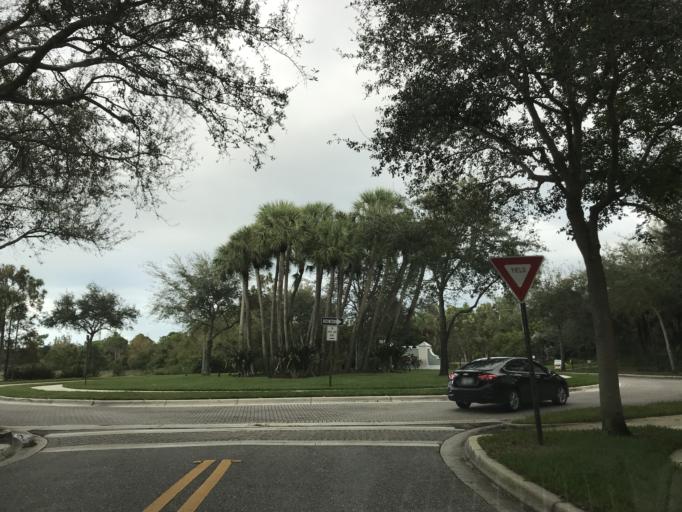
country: US
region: Florida
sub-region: Palm Beach County
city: Jupiter
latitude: 26.9164
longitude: -80.0955
